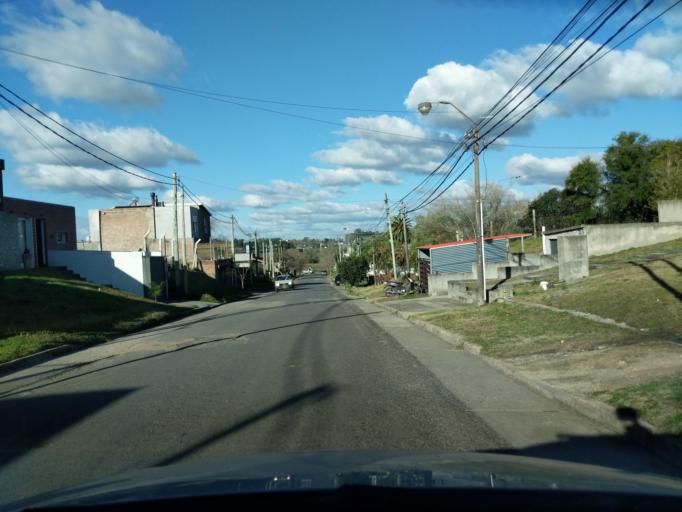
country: UY
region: Florida
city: Florida
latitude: -34.0897
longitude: -56.2110
